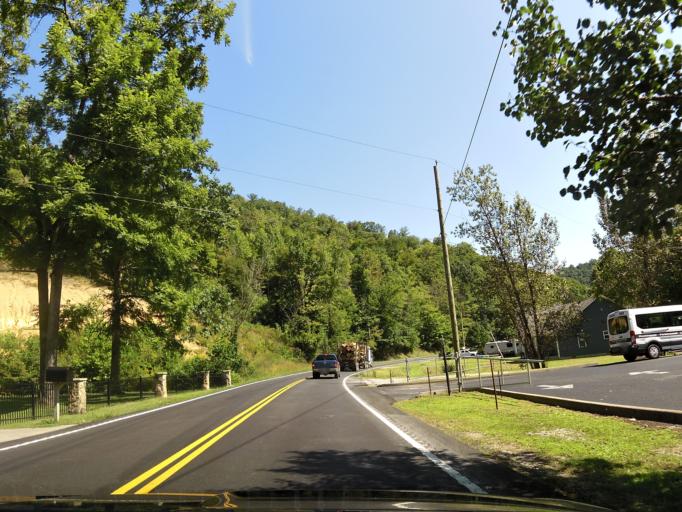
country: US
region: Kentucky
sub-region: Leslie County
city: Hyden
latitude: 37.1407
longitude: -83.4366
